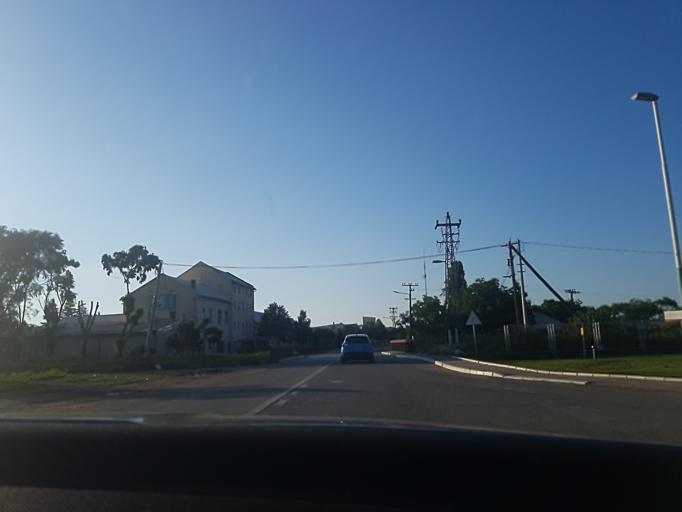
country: RS
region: Autonomna Pokrajina Vojvodina
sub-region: Juznobanatski Okrug
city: Vrsac
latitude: 45.1323
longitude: 21.2871
